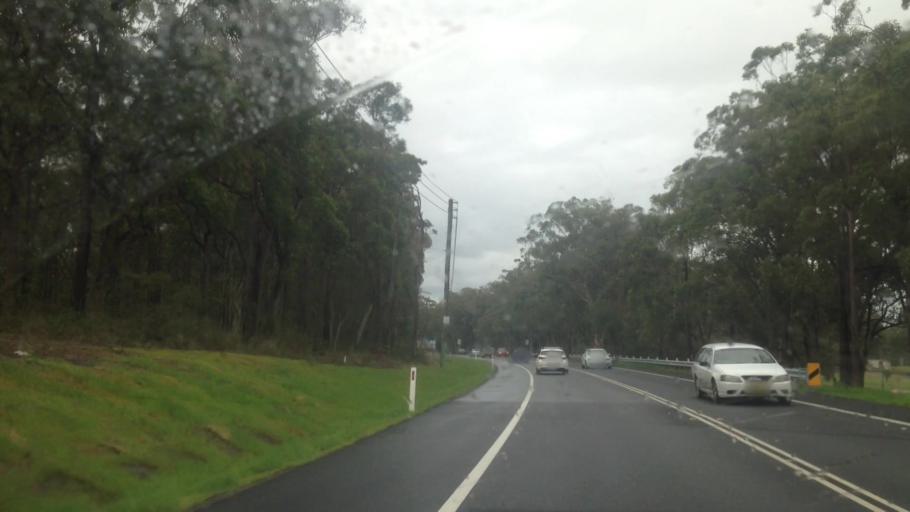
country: AU
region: New South Wales
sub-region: Lake Macquarie Shire
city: Dora Creek
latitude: -33.1205
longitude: 151.4774
